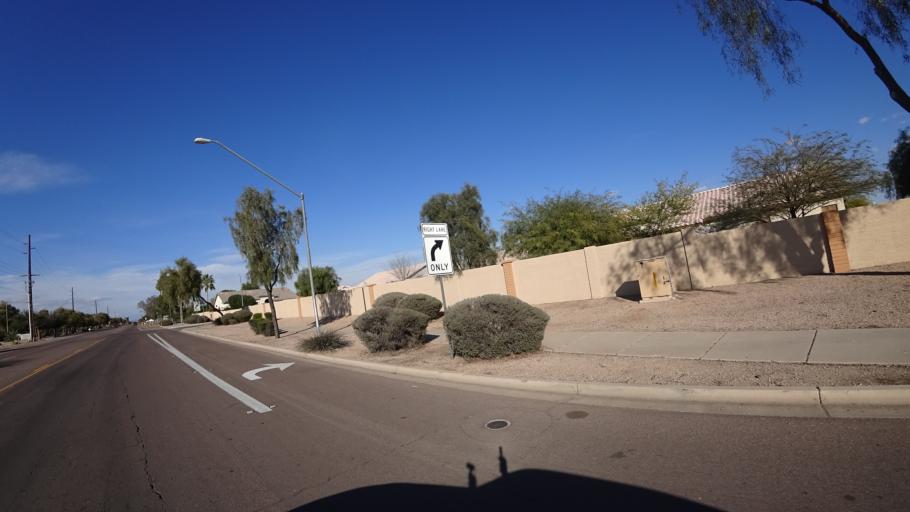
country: US
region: Arizona
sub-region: Maricopa County
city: Peoria
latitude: 33.5387
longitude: -112.2376
